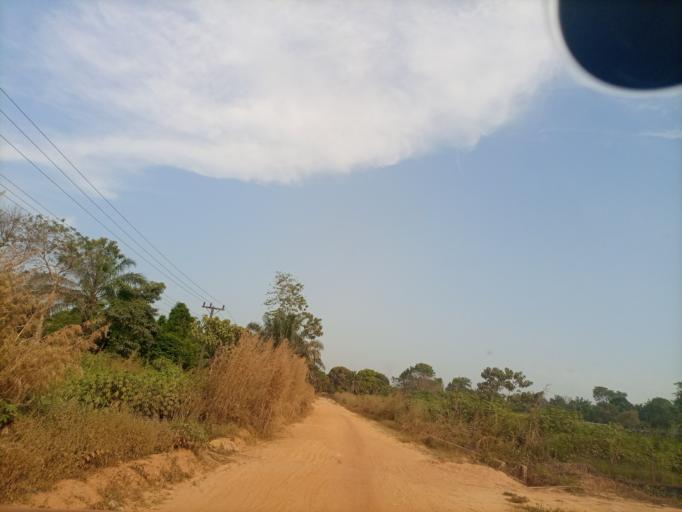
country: NG
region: Enugu
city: Obolo-Eke (1)
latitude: 6.8093
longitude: 7.5504
